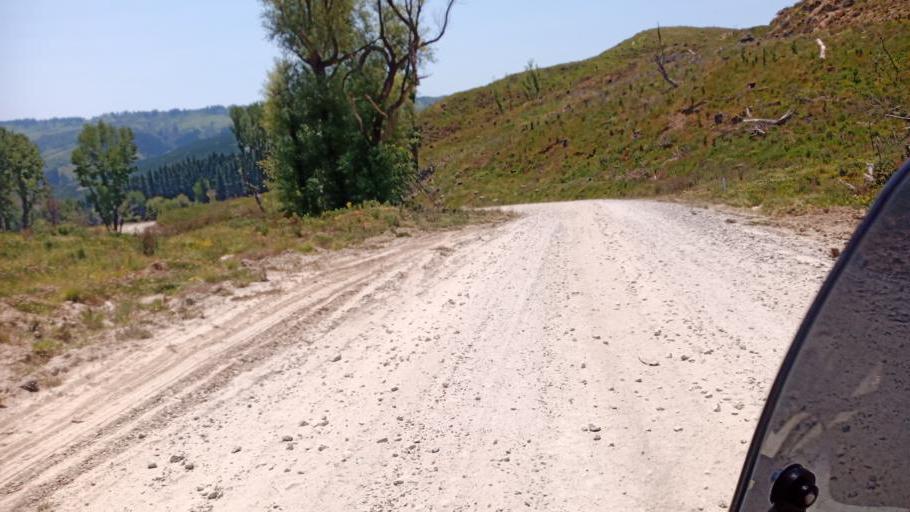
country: NZ
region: Gisborne
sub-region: Gisborne District
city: Gisborne
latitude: -38.2907
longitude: 178.0067
